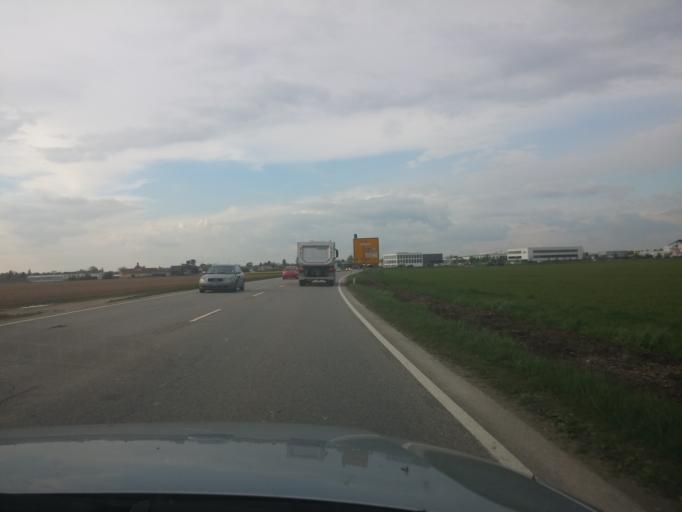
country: DE
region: Bavaria
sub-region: Upper Bavaria
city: Feldkirchen
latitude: 48.1356
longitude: 11.7362
